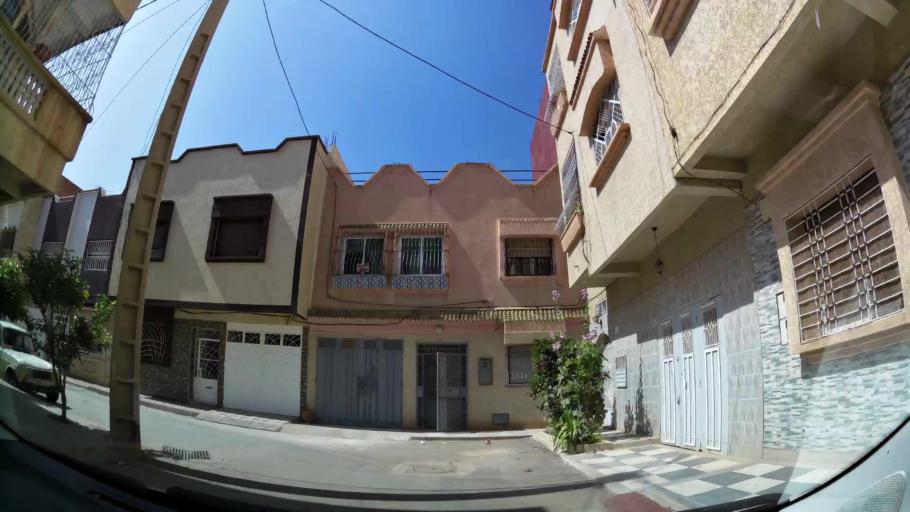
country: MA
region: Oriental
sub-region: Oujda-Angad
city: Oujda
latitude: 34.6888
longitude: -1.8710
